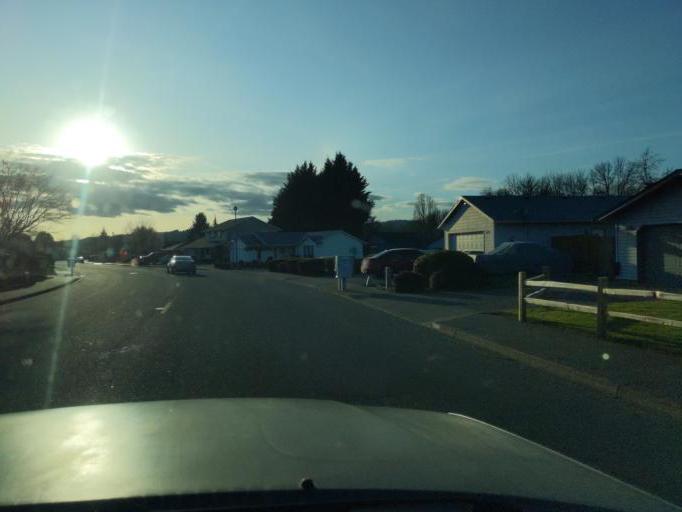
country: US
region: Oregon
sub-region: Yamhill County
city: McMinnville
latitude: 45.2024
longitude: -123.2126
